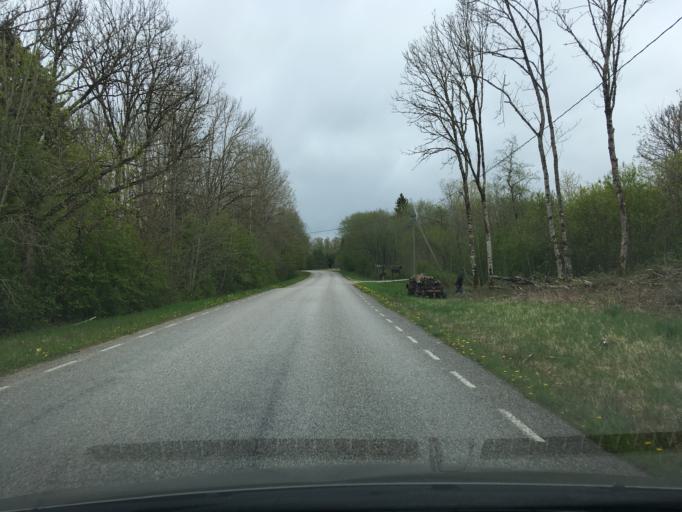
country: EE
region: Harju
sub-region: Rae vald
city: Vaida
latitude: 59.3495
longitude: 24.9993
